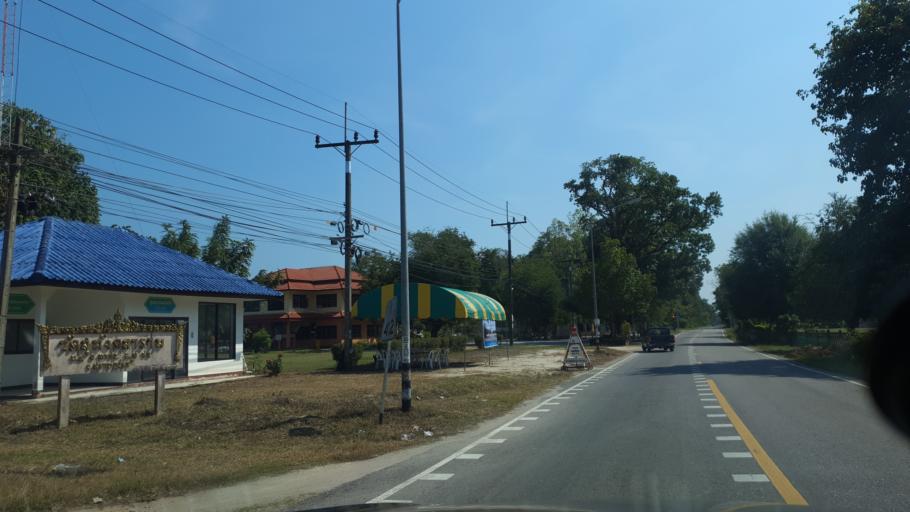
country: TH
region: Surat Thani
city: Tha Chana
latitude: 9.5867
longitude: 99.2019
